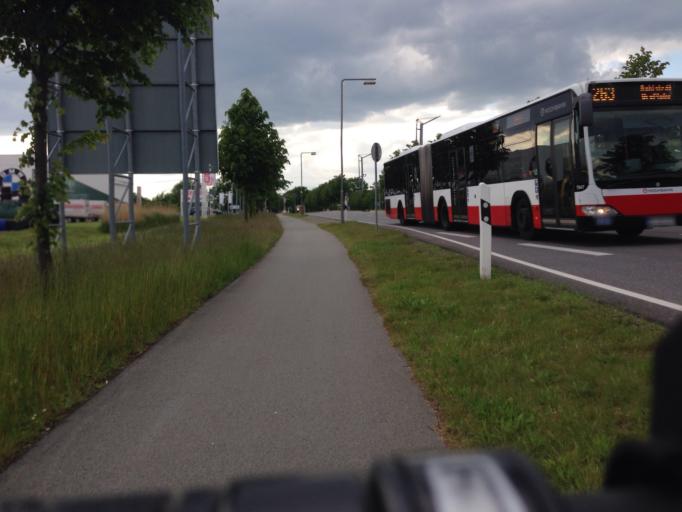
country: DE
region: Schleswig-Holstein
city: Barsbuettel
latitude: 53.5764
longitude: 10.1957
